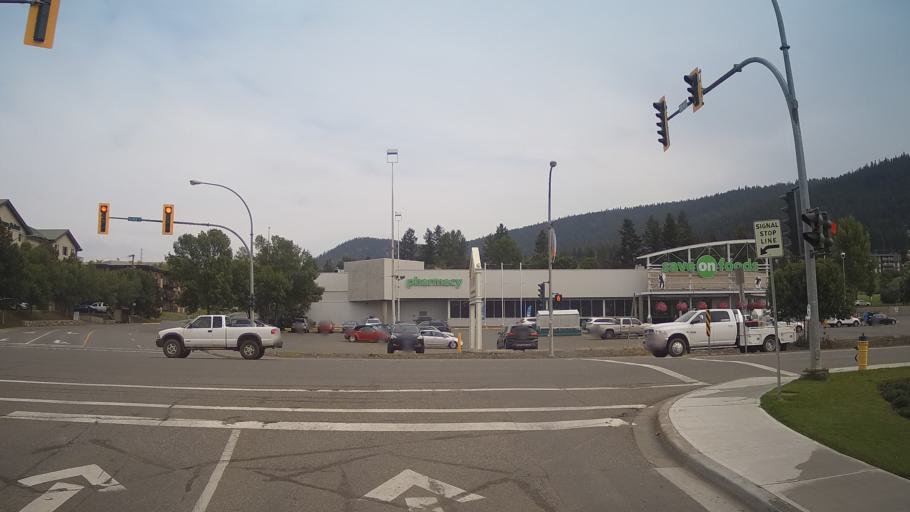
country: CA
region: British Columbia
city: Williams Lake
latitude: 52.1282
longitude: -122.1357
